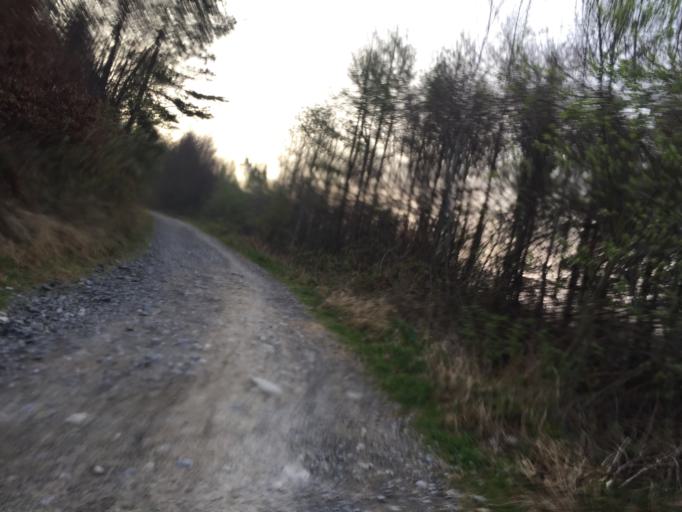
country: CH
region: Bern
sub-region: Bern-Mittelland District
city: Koniz
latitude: 46.9177
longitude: 7.4345
